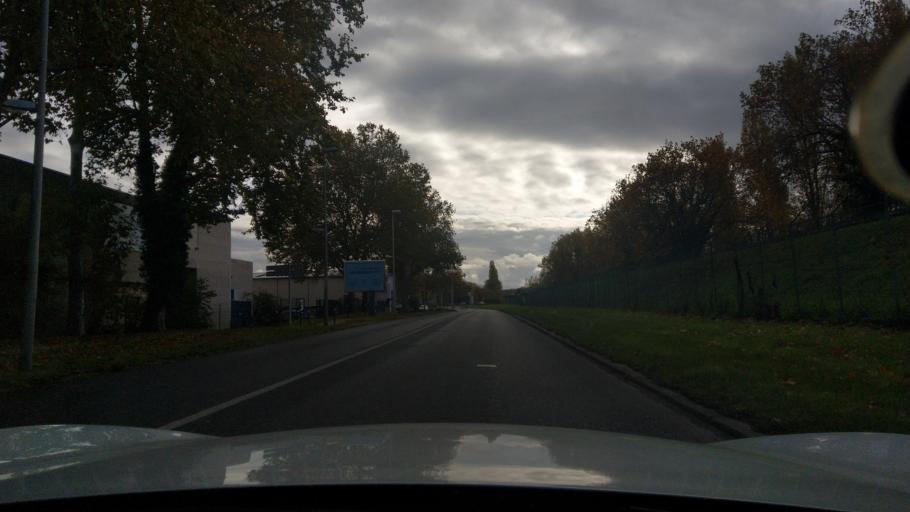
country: FR
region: Ile-de-France
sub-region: Departement de l'Essonne
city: Courcouronnes
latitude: 48.6320
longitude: 2.3961
